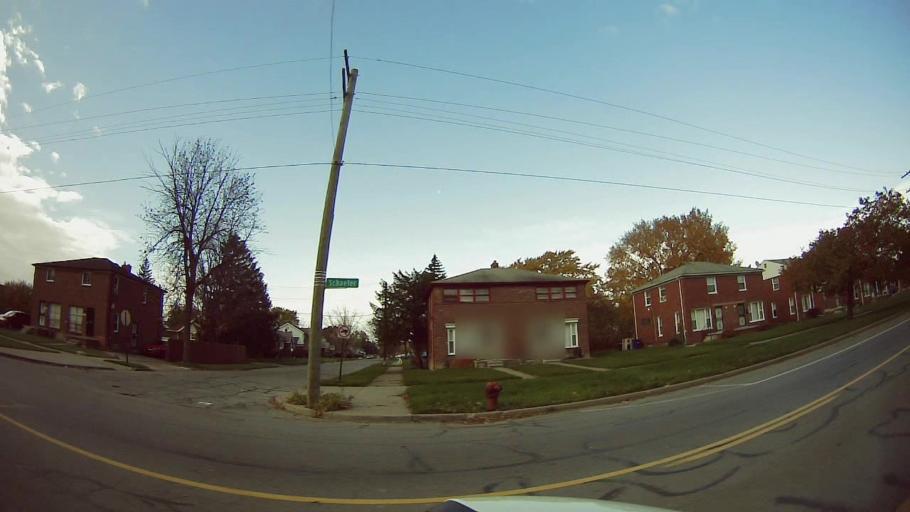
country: US
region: Michigan
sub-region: Wayne County
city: Dearborn
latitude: 42.3747
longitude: -83.1780
